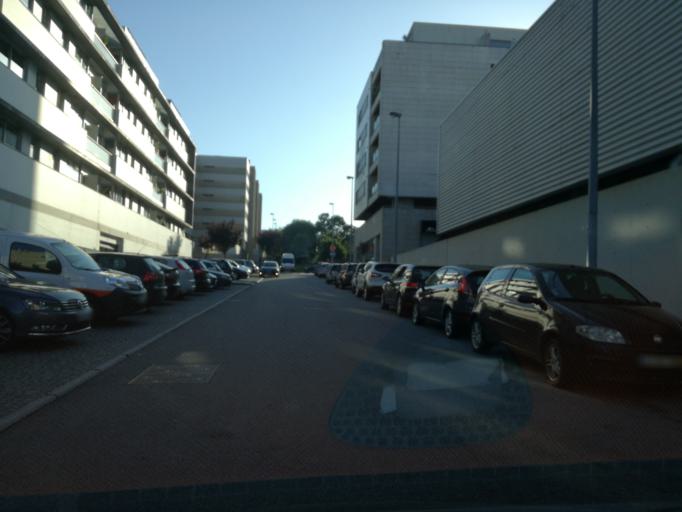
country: PT
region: Porto
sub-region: Maia
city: Leca do Bailio
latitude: 41.2248
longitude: -8.6126
